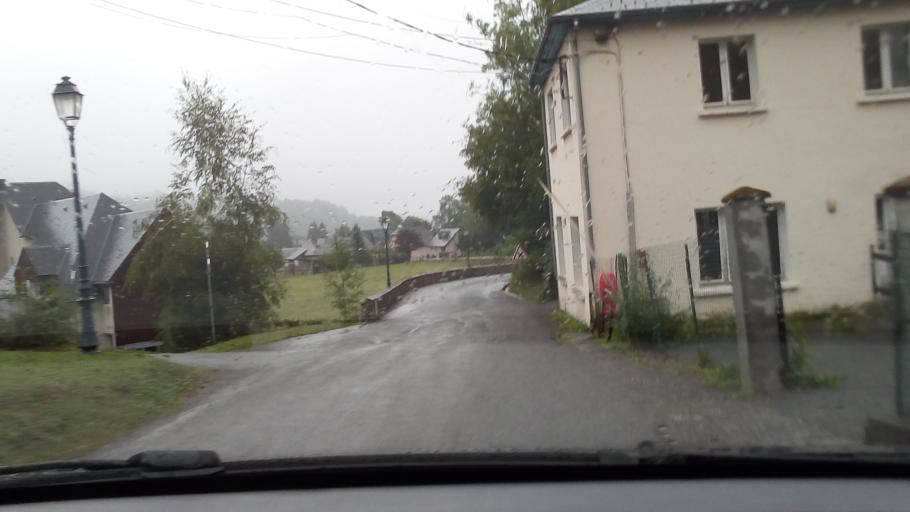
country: FR
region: Midi-Pyrenees
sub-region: Departement des Hautes-Pyrenees
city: Cauterets
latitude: 42.9511
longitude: -0.2163
